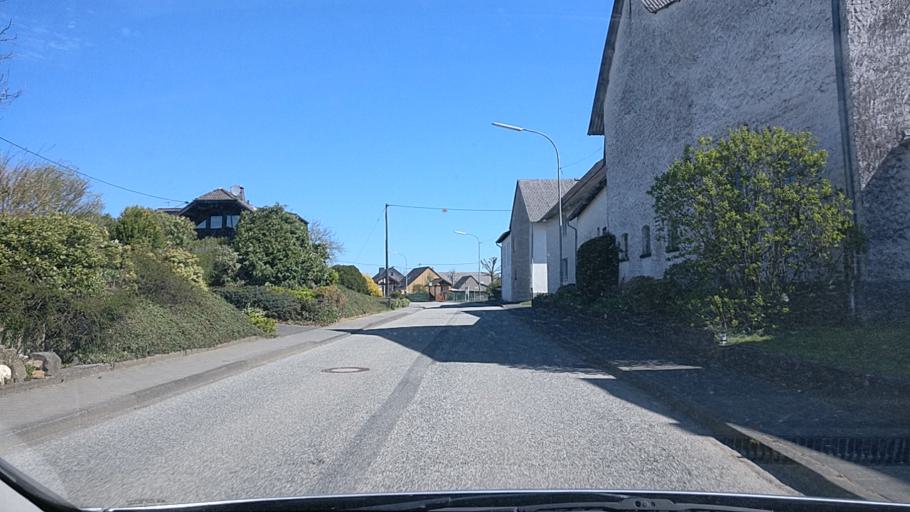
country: DE
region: Rheinland-Pfalz
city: Peterslahr
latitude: 50.6328
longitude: 7.4597
